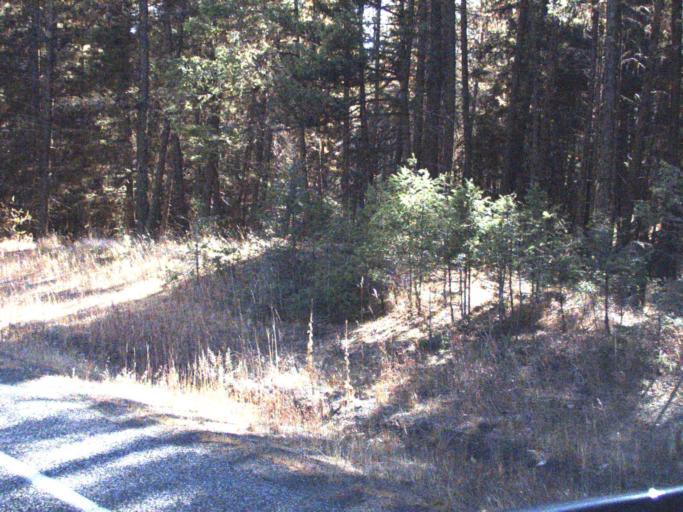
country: US
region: Washington
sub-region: Ferry County
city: Republic
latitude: 48.6552
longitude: -118.8038
